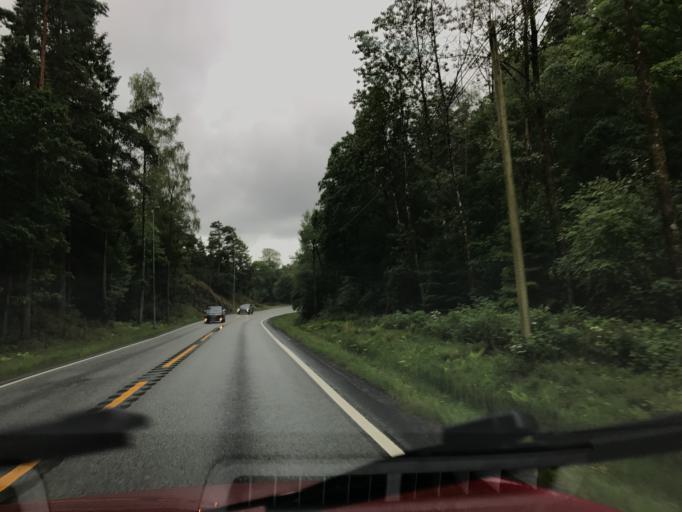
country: NO
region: Vest-Agder
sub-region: Mandal
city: Mandal
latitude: 58.0475
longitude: 7.5630
